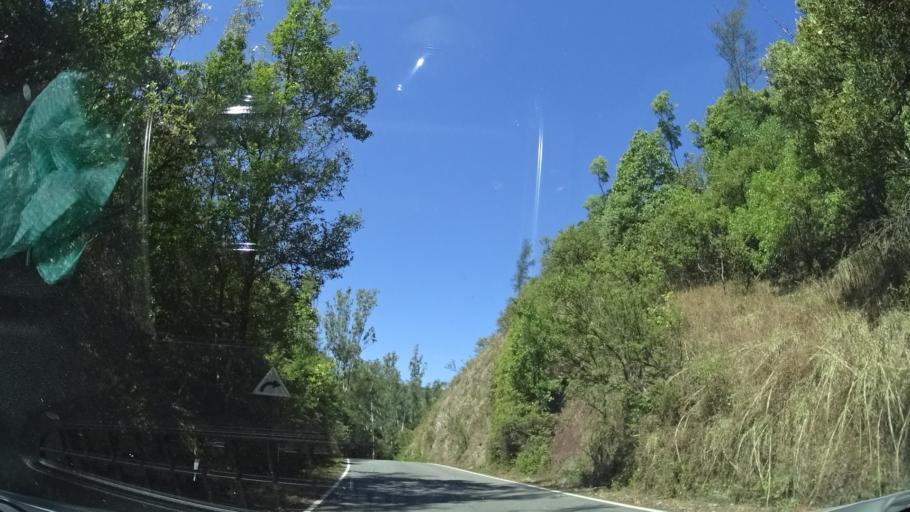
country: IN
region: Karnataka
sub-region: Udupi
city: Karkal
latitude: 13.2079
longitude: 75.1953
